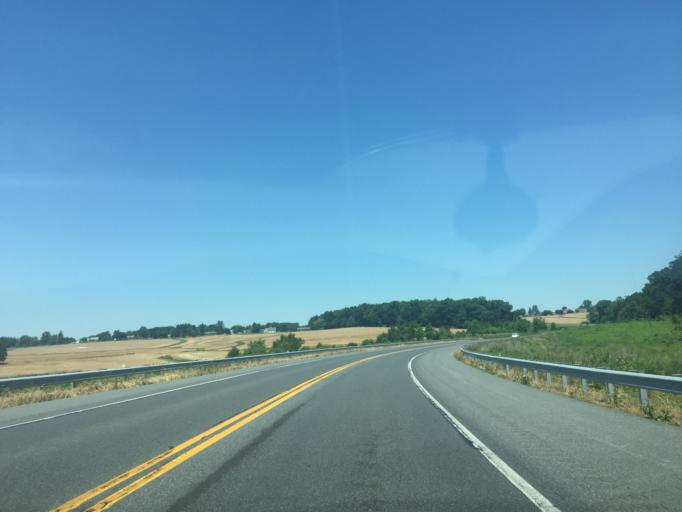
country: US
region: Maryland
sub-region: Carroll County
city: Hampstead
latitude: 39.5865
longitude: -76.8524
